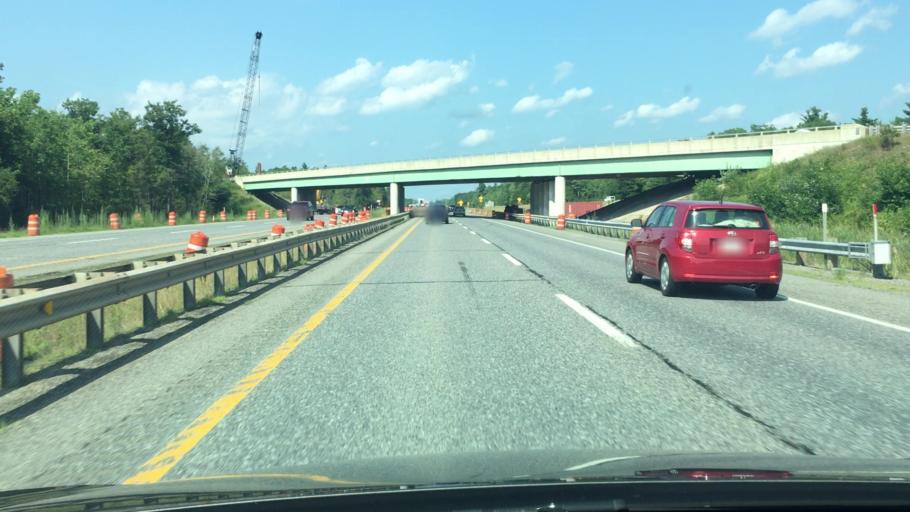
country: US
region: Maine
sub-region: Kennebec County
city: Gardiner
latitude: 44.2169
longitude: -69.8248
